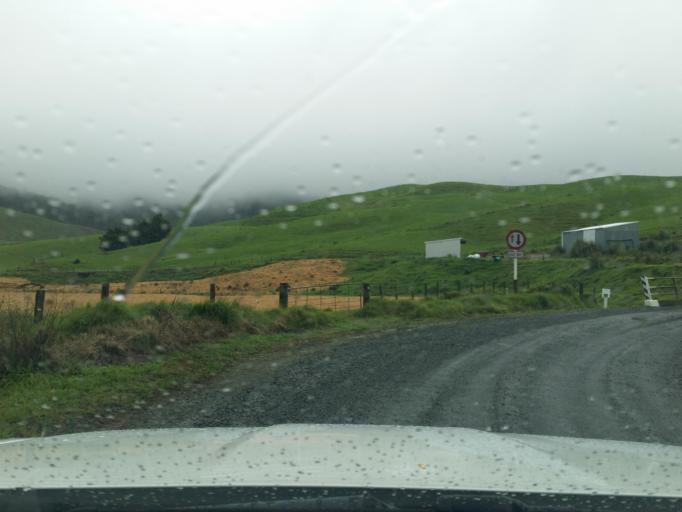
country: NZ
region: Northland
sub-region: Kaipara District
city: Dargaville
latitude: -35.7811
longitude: 173.9505
